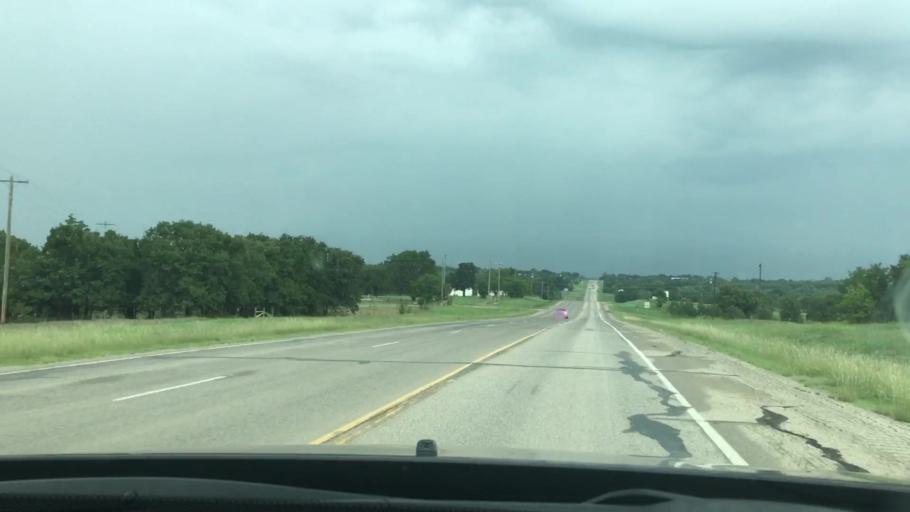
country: US
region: Oklahoma
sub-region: Carter County
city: Healdton
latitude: 34.2000
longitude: -97.4747
